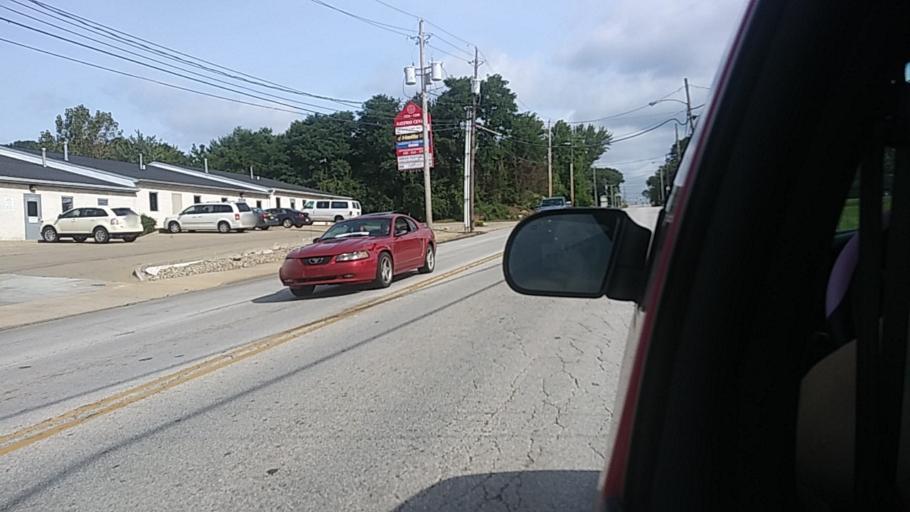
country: US
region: Ohio
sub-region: Summit County
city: Tallmadge
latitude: 41.0961
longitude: -81.4665
